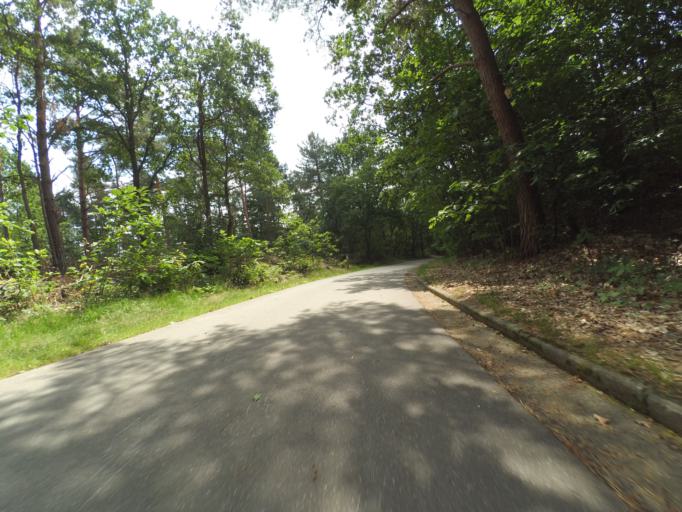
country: BE
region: Flanders
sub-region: Provincie Limburg
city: Kinrooi
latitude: 51.0748
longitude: 5.6889
